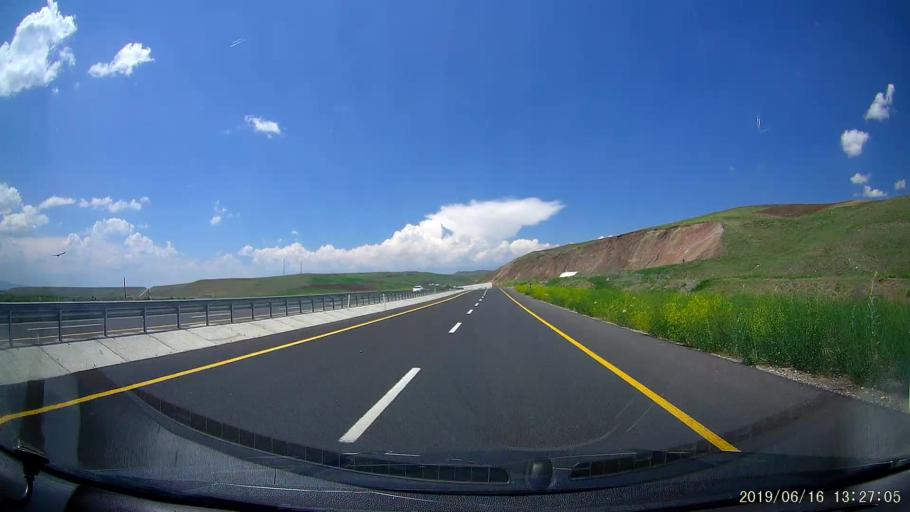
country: TR
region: Agri
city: Taslicay
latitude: 39.6666
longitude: 43.3161
